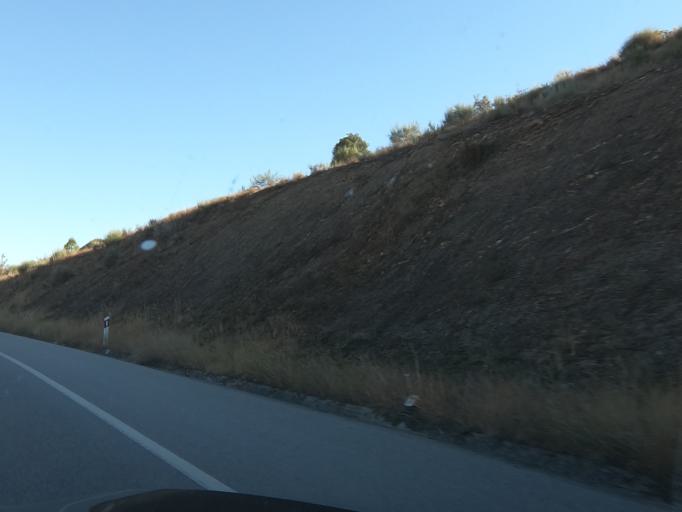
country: PT
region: Braganca
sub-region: Mirandela
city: Mirandela
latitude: 41.5202
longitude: -7.2391
